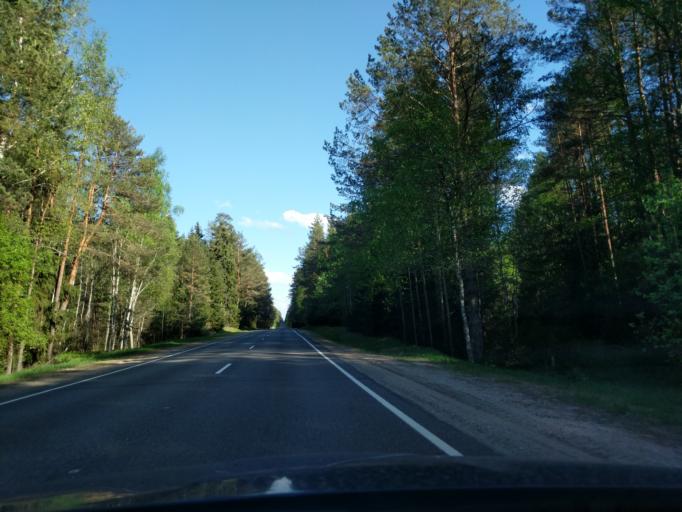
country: BY
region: Minsk
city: Myadzyel
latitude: 54.8062
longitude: 26.9905
